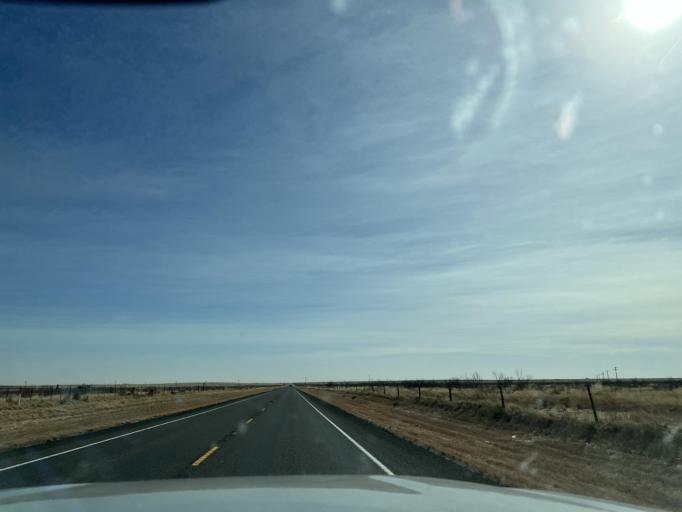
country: US
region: Texas
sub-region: Andrews County
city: Andrews
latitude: 32.4876
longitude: -102.4836
